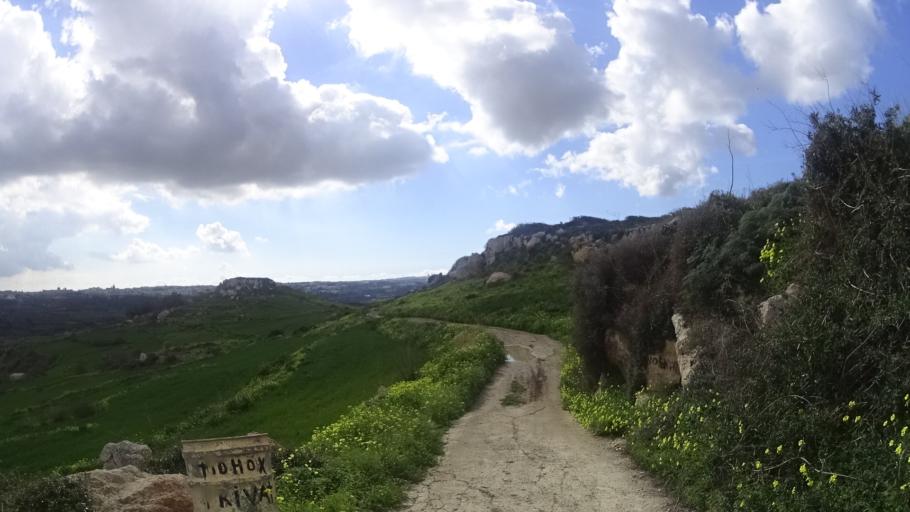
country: MT
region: L-Imtarfa
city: Imtarfa
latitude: 35.9022
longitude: 14.3841
